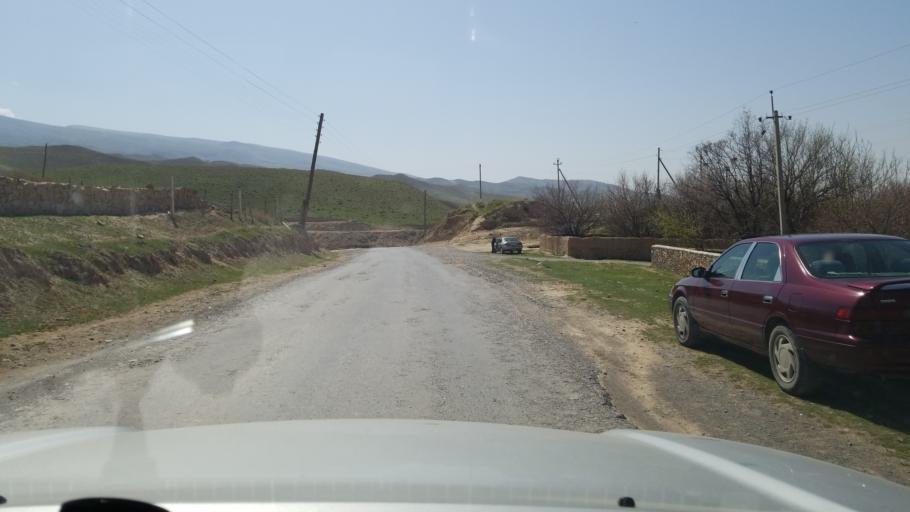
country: TM
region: Lebap
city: Gowurdak
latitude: 37.8886
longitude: 66.4611
